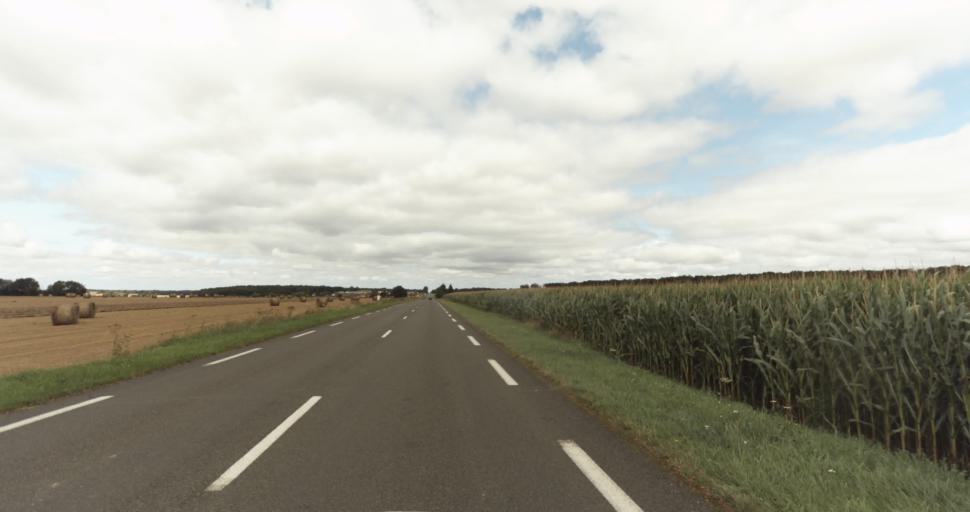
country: FR
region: Haute-Normandie
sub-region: Departement de l'Eure
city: Arnieres-sur-Iton
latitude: 48.9474
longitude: 1.1632
